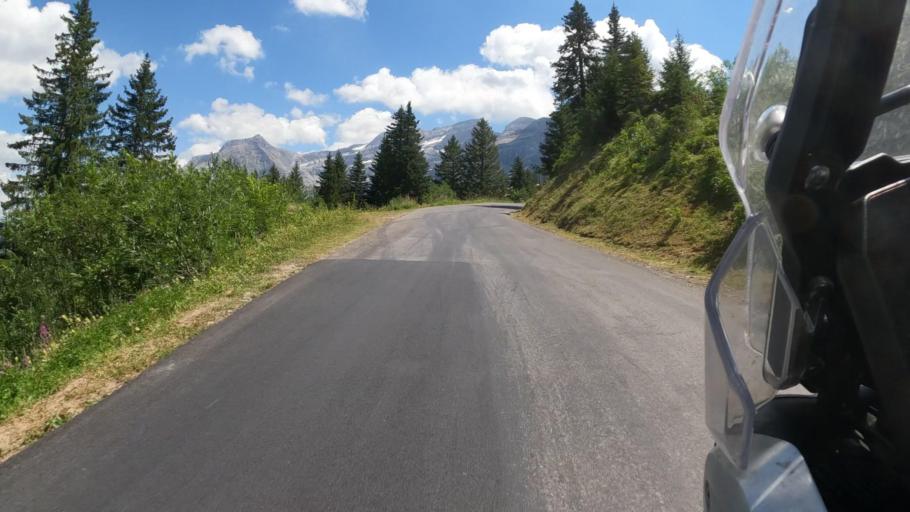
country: CH
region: Vaud
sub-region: Aigle District
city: Villars-sur-Ollon
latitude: 46.3261
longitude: 7.1259
